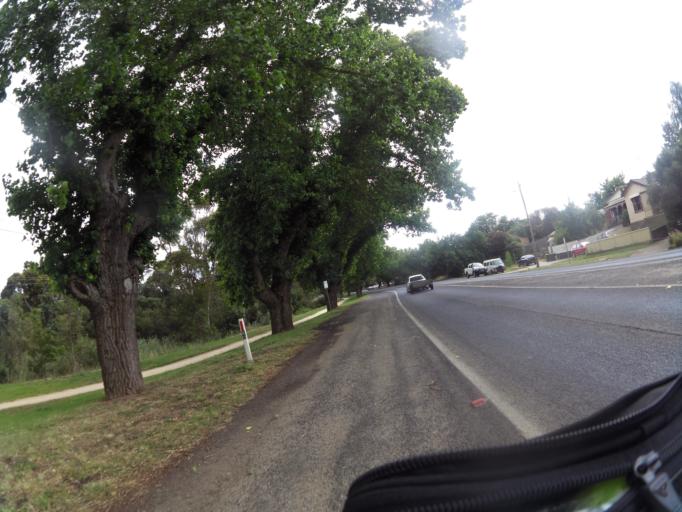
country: AU
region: Victoria
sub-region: Mount Alexander
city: Castlemaine
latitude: -37.0721
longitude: 144.2086
